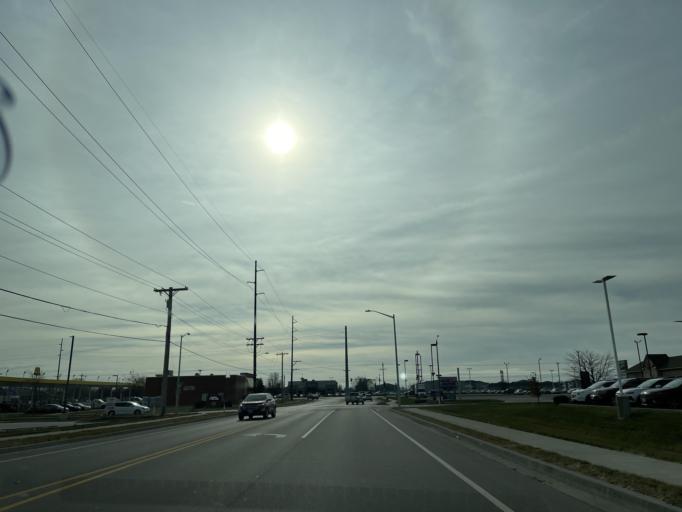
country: US
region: Illinois
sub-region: Sangamon County
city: Jerome
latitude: 39.7581
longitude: -89.7344
